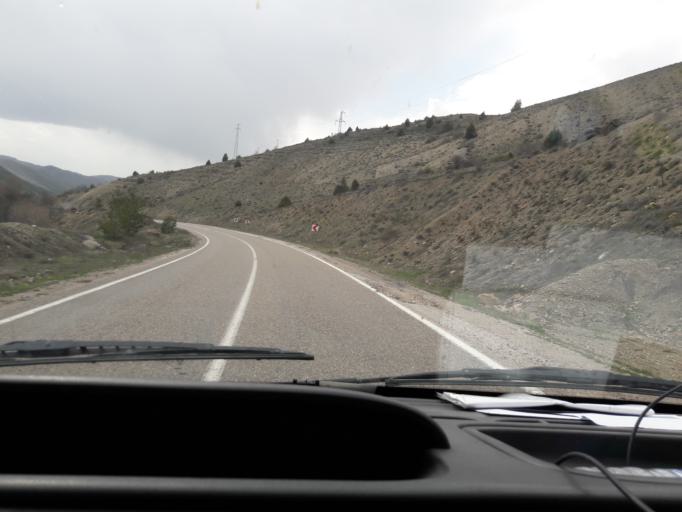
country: TR
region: Giresun
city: Alucra
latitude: 40.2733
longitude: 38.8673
